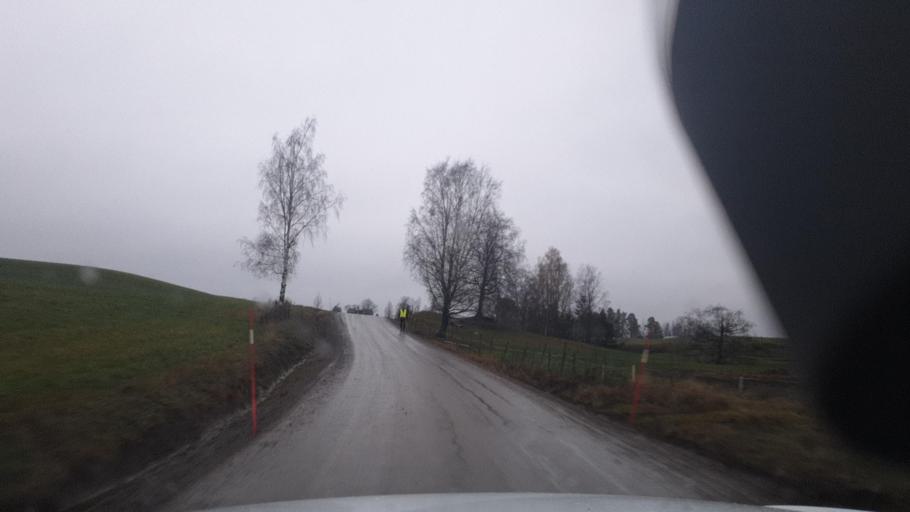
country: SE
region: Vaermland
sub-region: Eda Kommun
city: Amotfors
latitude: 59.7210
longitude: 12.1435
